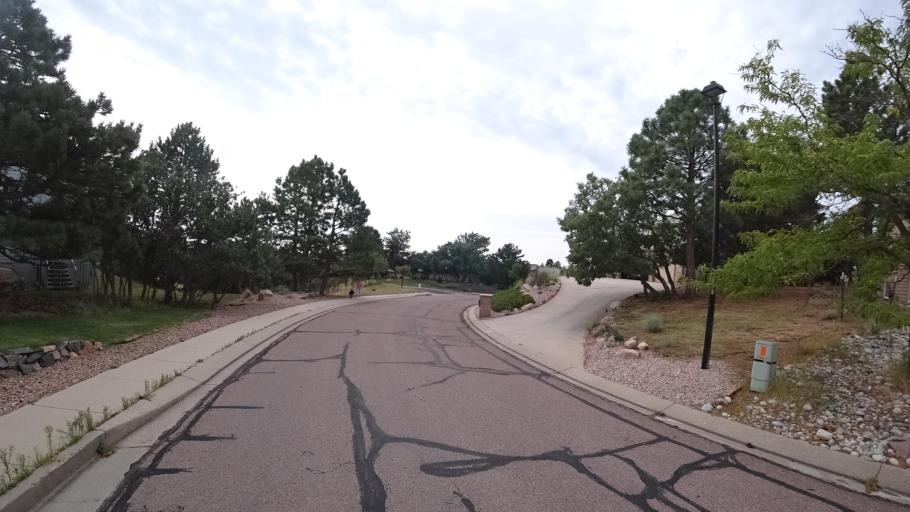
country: US
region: Colorado
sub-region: El Paso County
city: Air Force Academy
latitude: 38.9388
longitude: -104.8647
